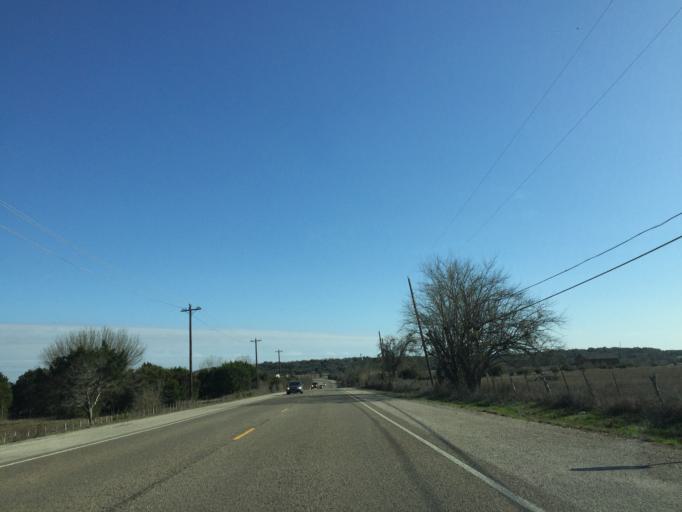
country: US
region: Texas
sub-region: Williamson County
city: Florence
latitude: 30.7714
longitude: -97.8479
